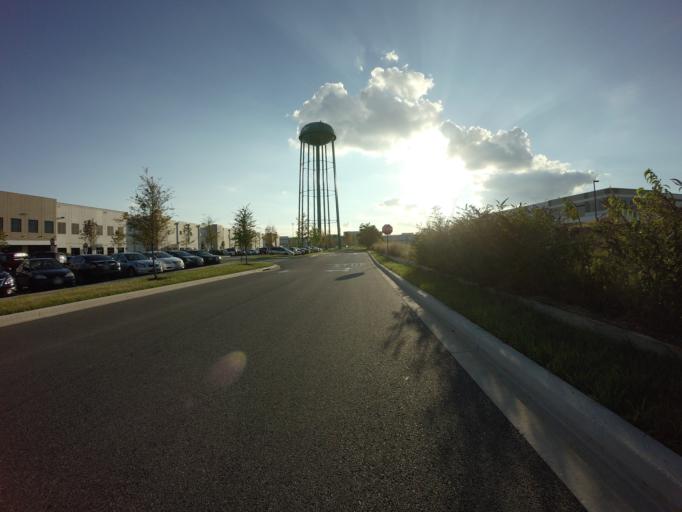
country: US
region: Maryland
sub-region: Baltimore County
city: Dundalk
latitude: 39.2688
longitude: -76.5493
